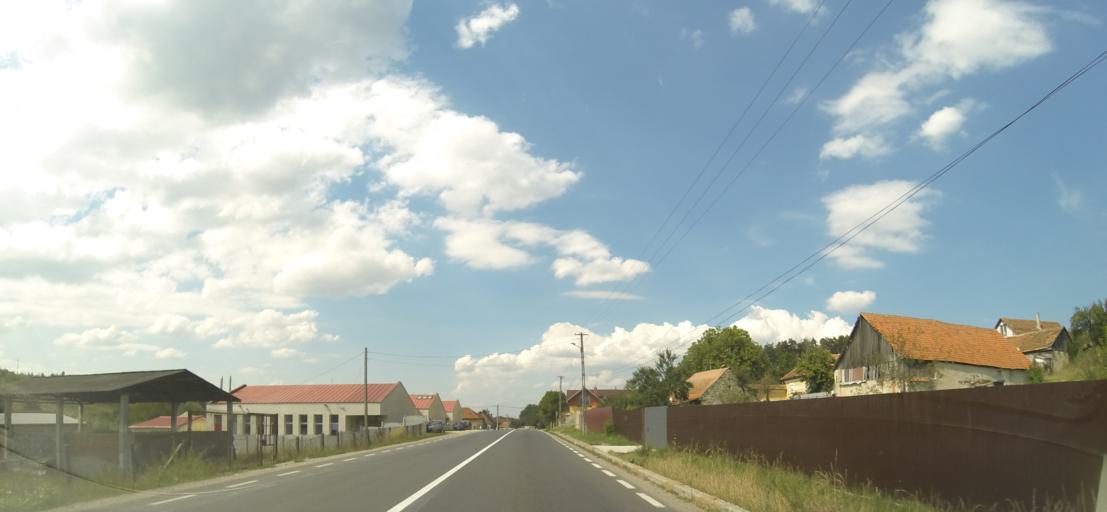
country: RO
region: Brasov
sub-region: Comuna Sinca Veche
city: Persani
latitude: 45.7783
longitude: 25.2162
